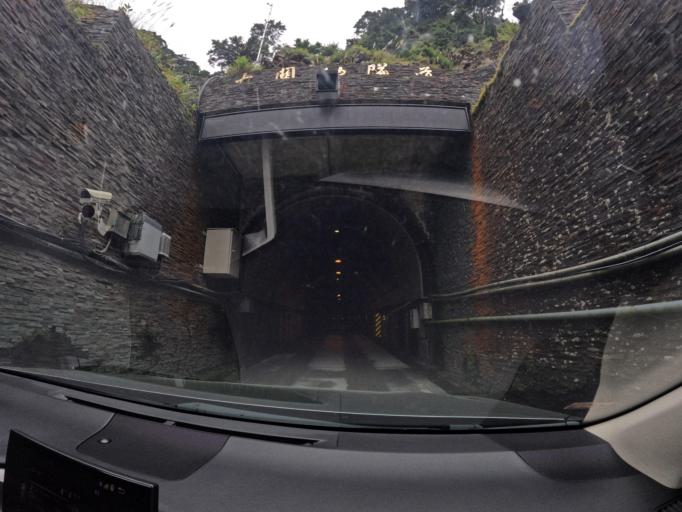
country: TW
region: Taiwan
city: Yujing
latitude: 23.2656
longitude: 120.9553
